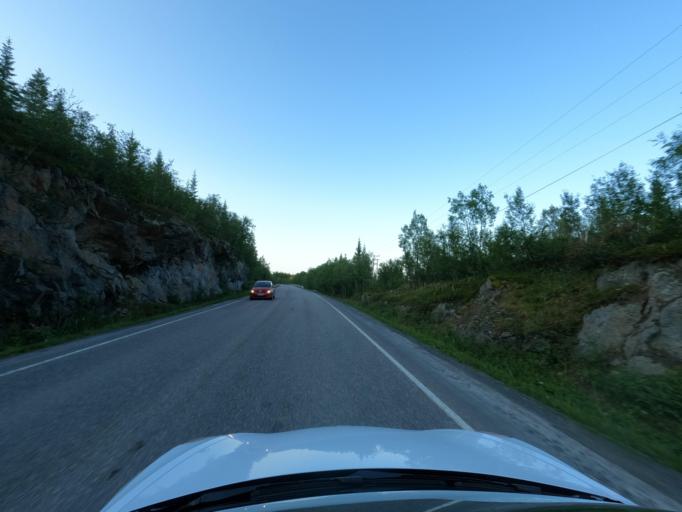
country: NO
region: Troms
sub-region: Harstad
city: Harstad
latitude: 68.7223
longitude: 16.5331
